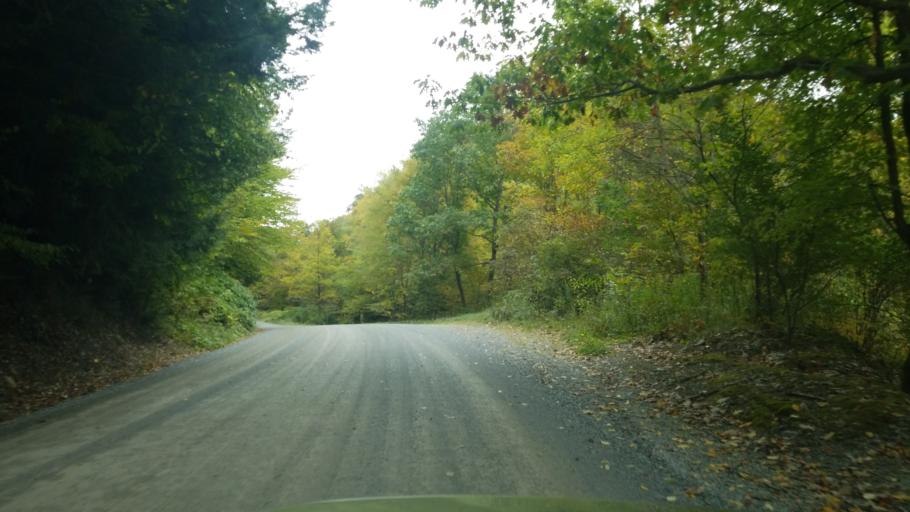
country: US
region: Pennsylvania
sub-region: Clearfield County
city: Curwensville
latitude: 40.9658
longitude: -78.4898
